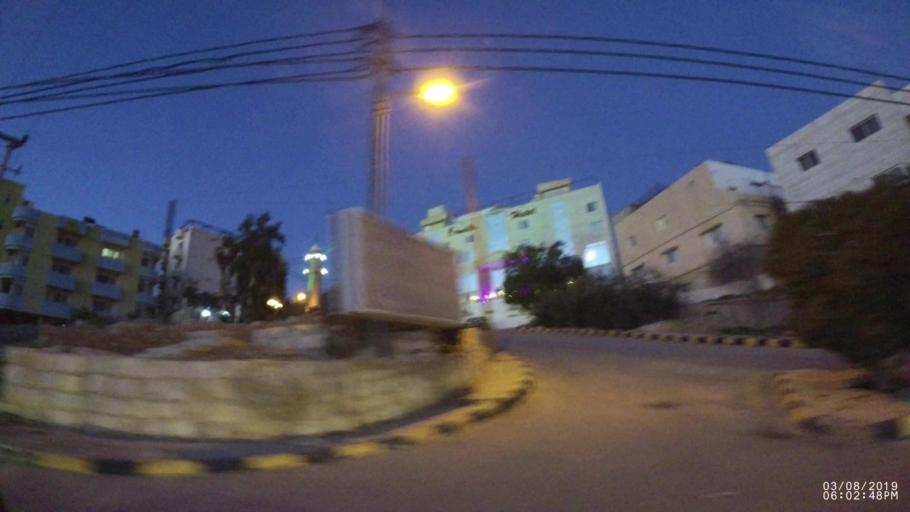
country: JO
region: Ma'an
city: Petra
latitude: 30.3263
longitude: 35.4711
